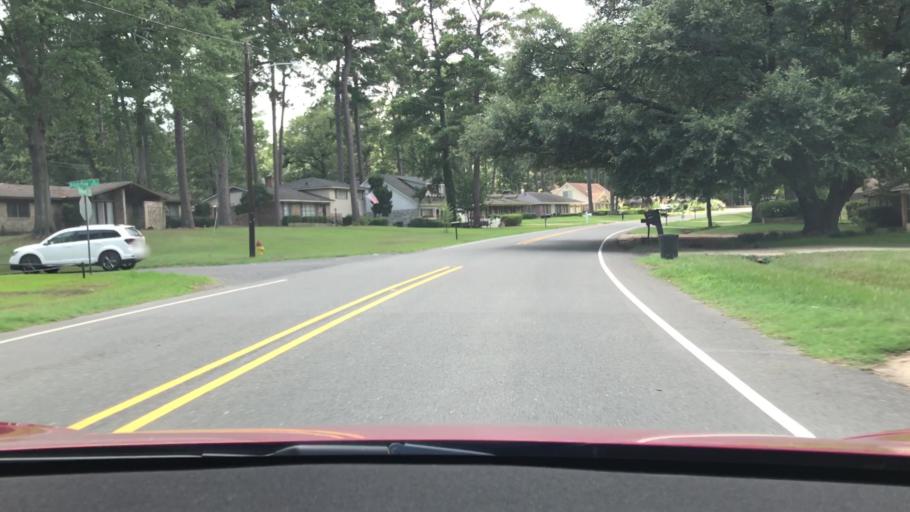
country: US
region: Louisiana
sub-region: De Soto Parish
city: Stonewall
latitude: 32.3892
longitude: -93.7921
